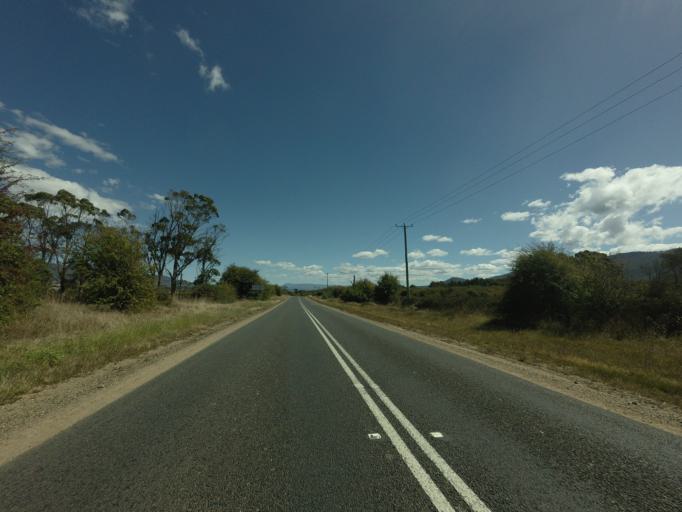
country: AU
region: Tasmania
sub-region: Break O'Day
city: St Helens
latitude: -41.5791
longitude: 148.1608
